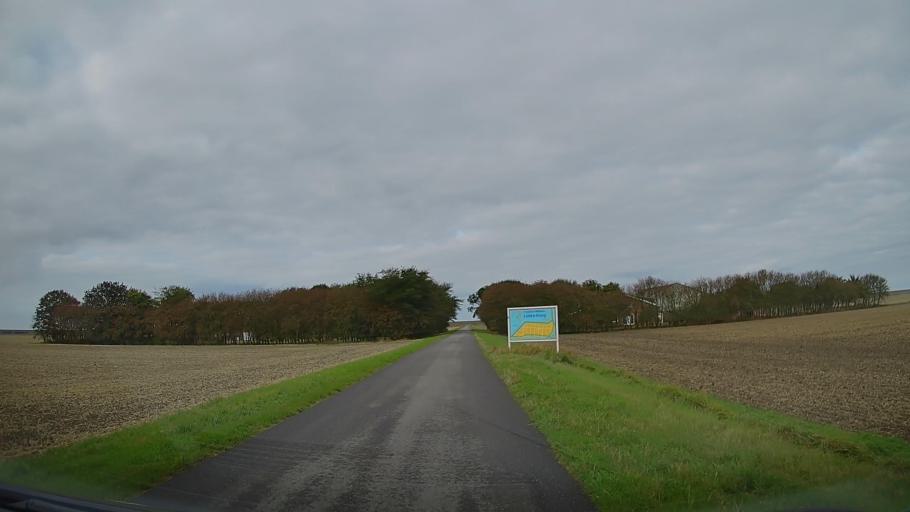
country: DE
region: Schleswig-Holstein
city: Friedrich-Wilhelm-Lubke-Koog
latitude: 54.8694
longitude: 8.6255
